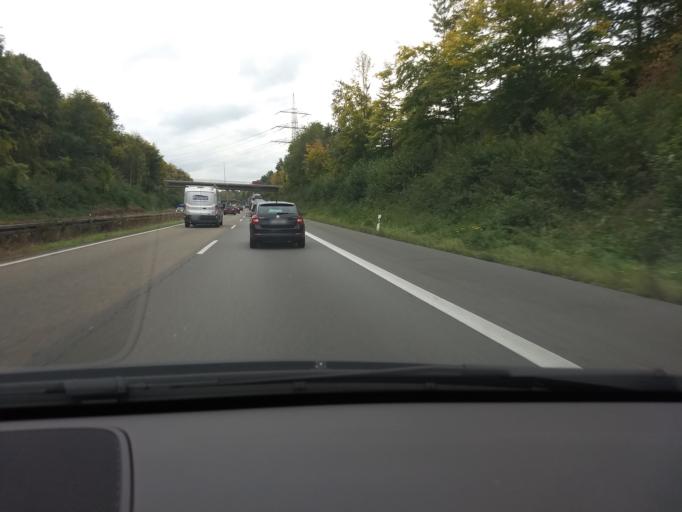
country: DE
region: North Rhine-Westphalia
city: Dorsten
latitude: 51.6483
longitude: 6.9320
